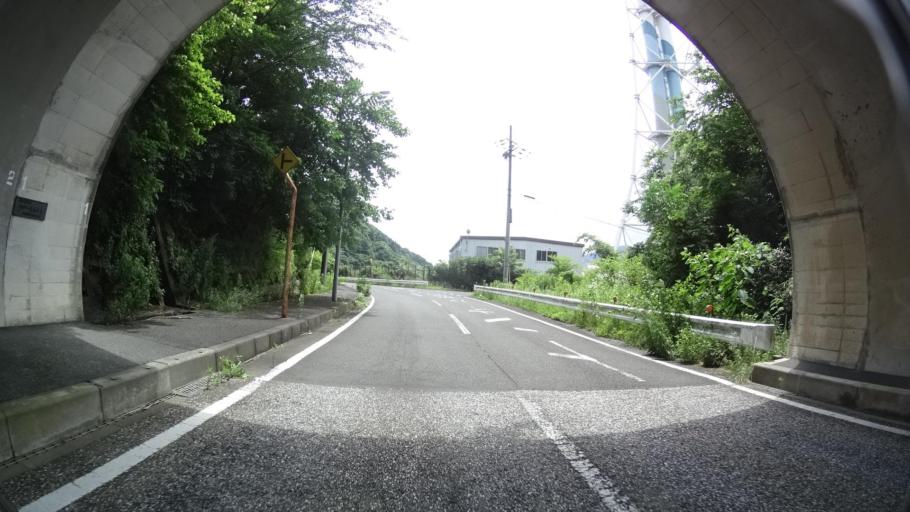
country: JP
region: Kyoto
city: Maizuru
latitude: 35.5329
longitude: 135.3469
